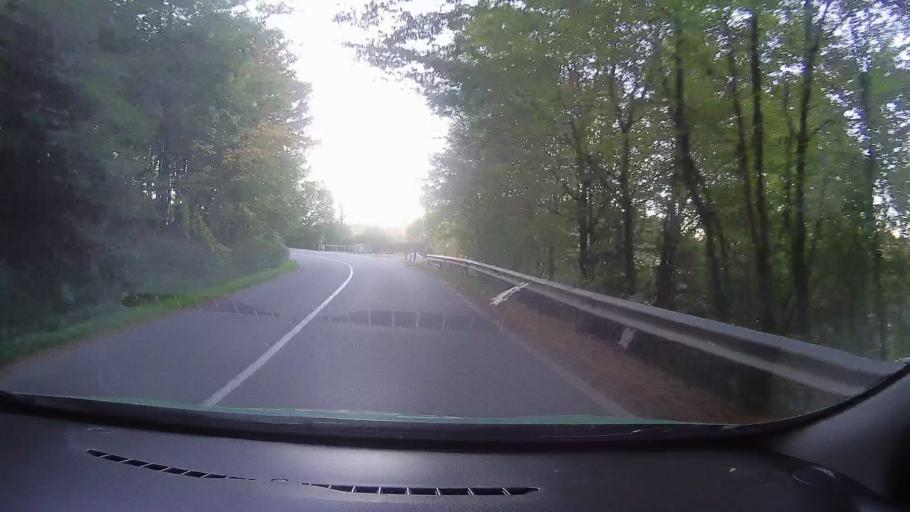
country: RO
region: Timis
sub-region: Comuna Fardea
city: Fardea
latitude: 45.7509
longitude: 22.1299
